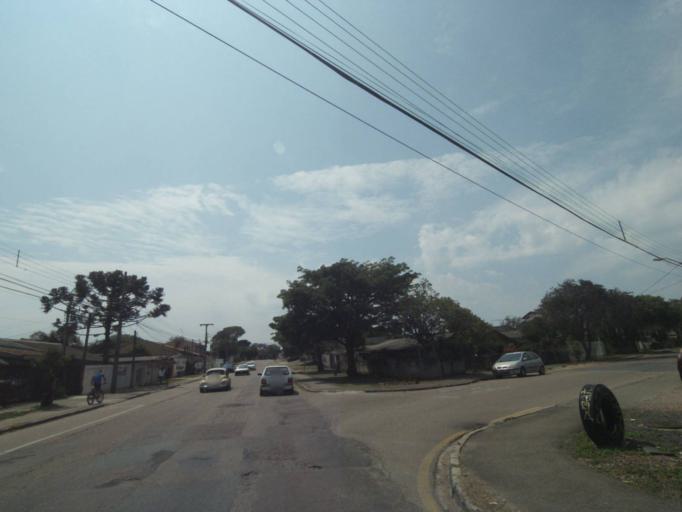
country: BR
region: Parana
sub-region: Curitiba
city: Curitiba
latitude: -25.4801
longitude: -49.3300
